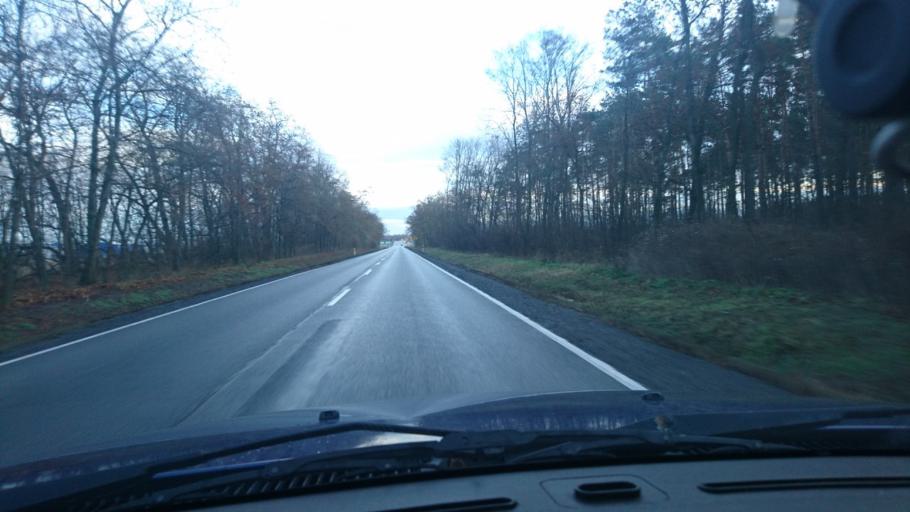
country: PL
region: Greater Poland Voivodeship
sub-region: Powiat kepinski
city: Kepno
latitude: 51.3222
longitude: 17.9708
